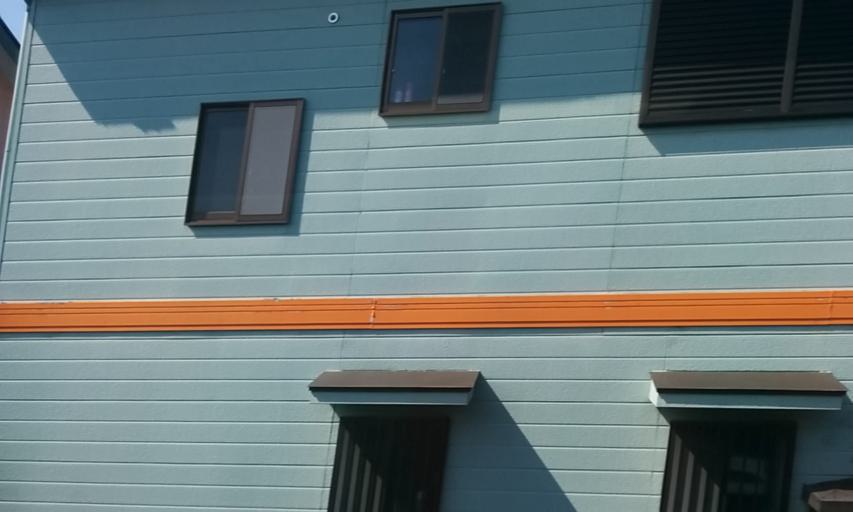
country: JP
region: Saitama
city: Kazo
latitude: 36.1217
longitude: 139.5988
